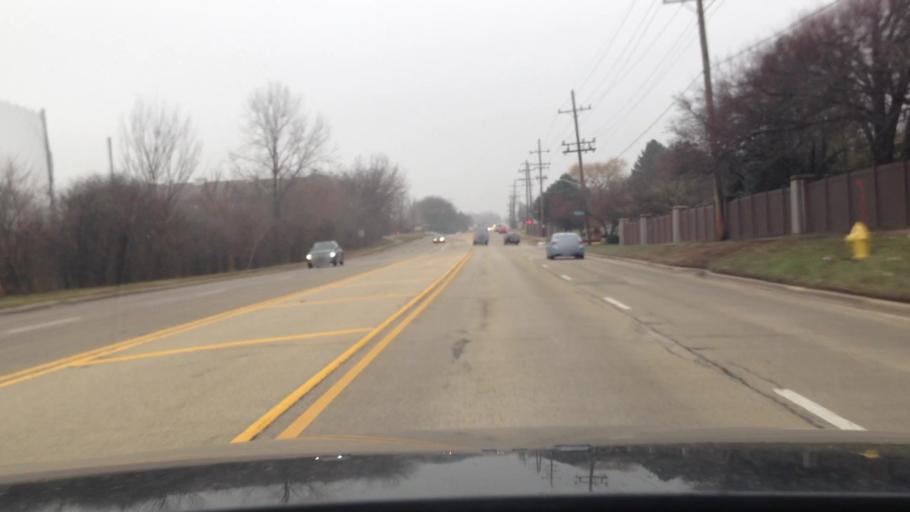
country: US
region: Illinois
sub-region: DuPage County
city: Westmont
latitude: 41.8193
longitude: -87.9764
